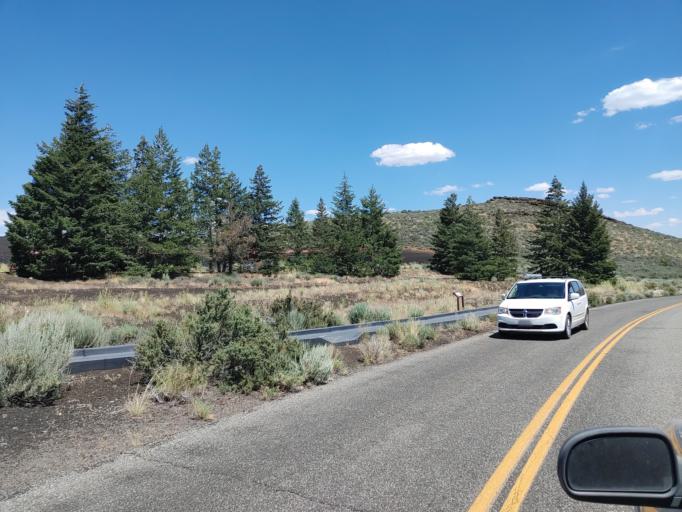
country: US
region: Idaho
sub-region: Butte County
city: Arco
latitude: 43.4619
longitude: -113.5601
